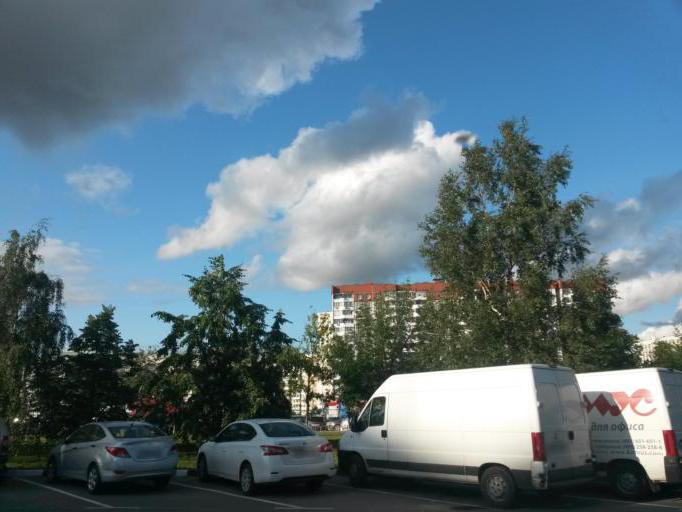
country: RU
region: Moscow
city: Zhulebino
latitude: 55.6854
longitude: 37.8529
